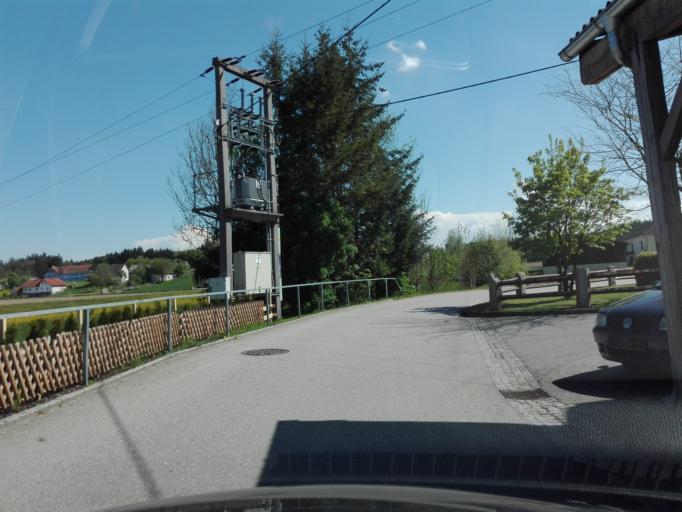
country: AT
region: Upper Austria
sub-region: Politischer Bezirk Grieskirchen
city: Bad Schallerbach
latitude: 48.3373
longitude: 13.8980
